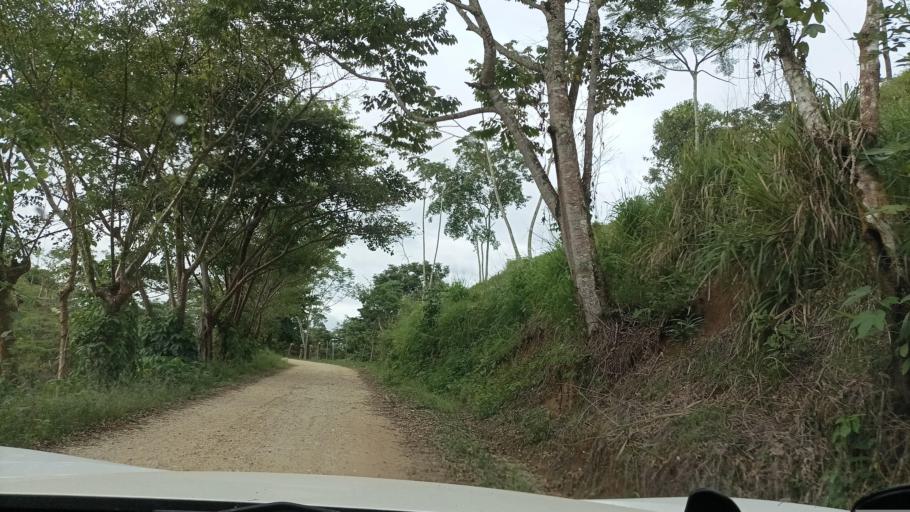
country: MX
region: Veracruz
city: Hidalgotitlan
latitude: 17.5870
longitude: -94.4217
